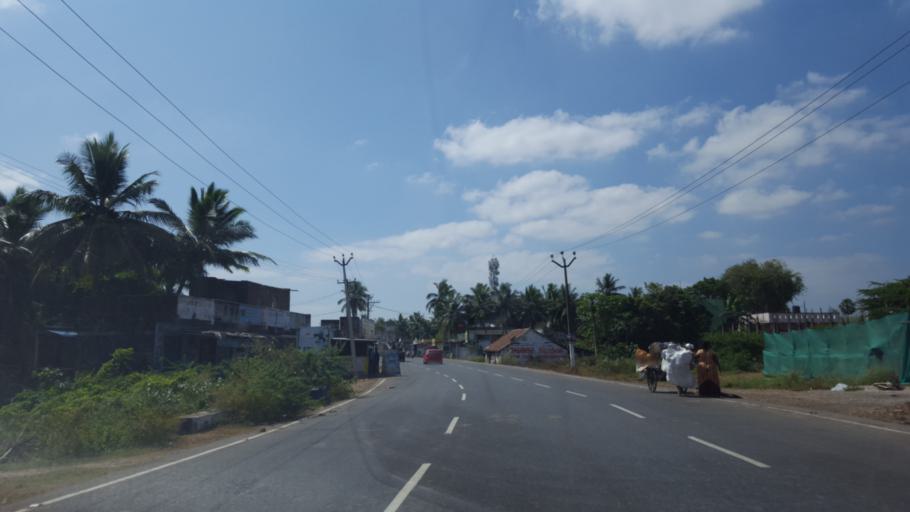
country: IN
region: Tamil Nadu
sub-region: Kancheepuram
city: Mamallapuram
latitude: 12.6488
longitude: 80.1746
